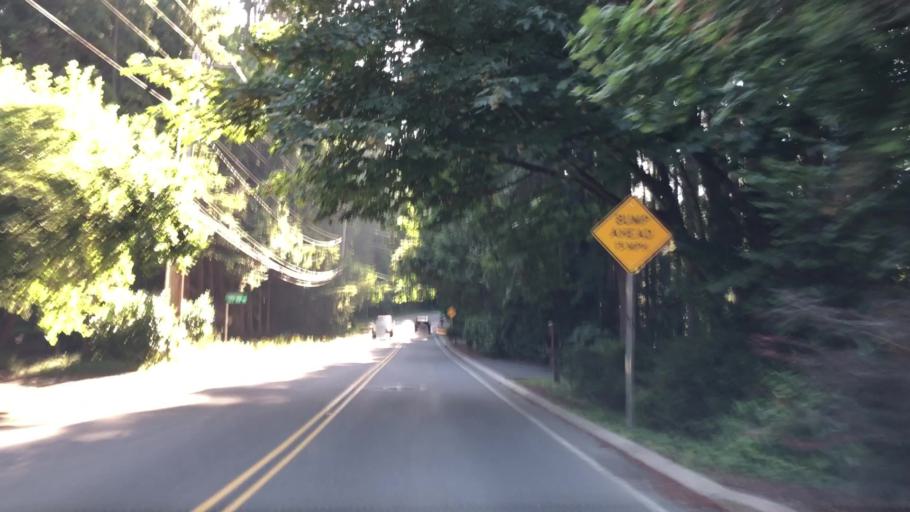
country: US
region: Washington
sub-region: King County
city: Woodinville
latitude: 47.7580
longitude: -122.1220
